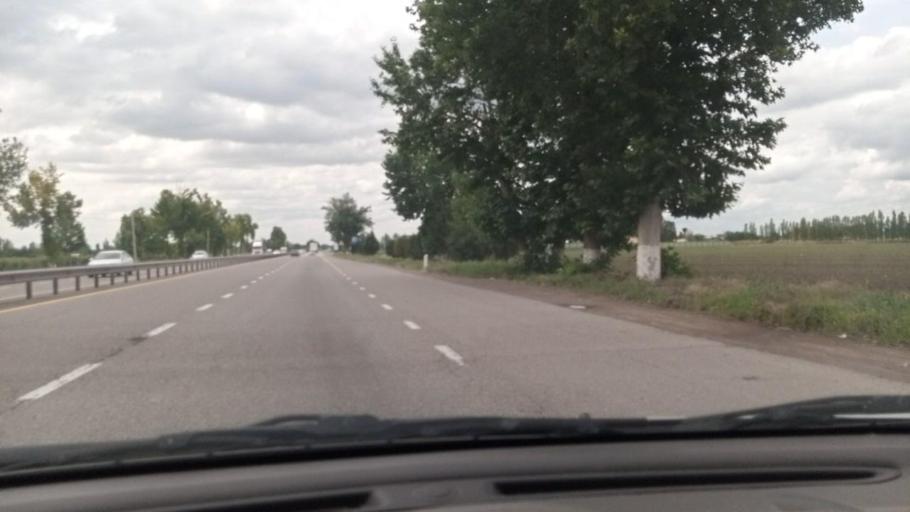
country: UZ
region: Toshkent Shahri
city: Bektemir
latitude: 41.1454
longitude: 69.4311
